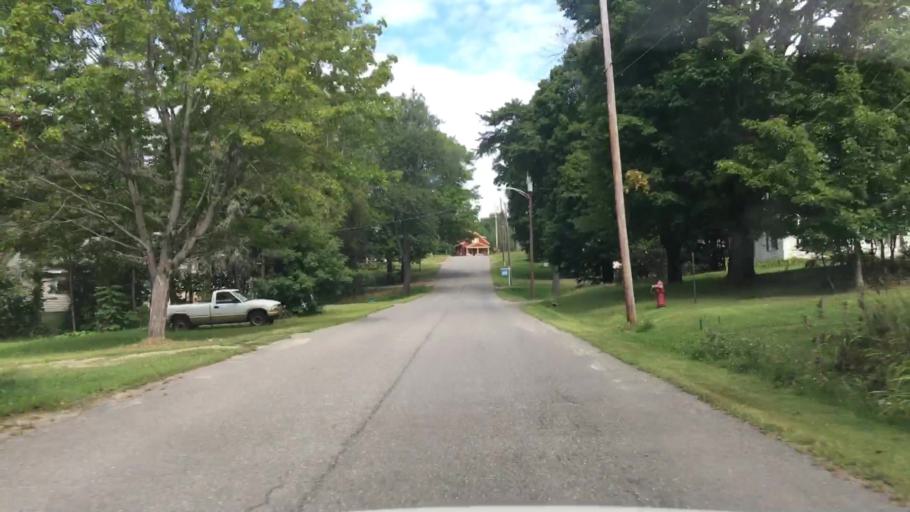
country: US
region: Maine
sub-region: Piscataquis County
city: Dover-Foxcroft
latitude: 45.1892
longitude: -69.2228
